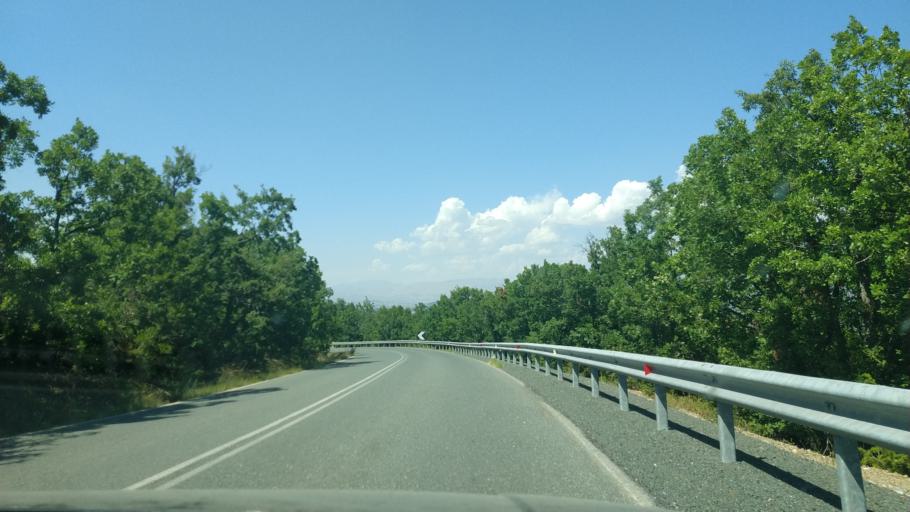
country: GR
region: West Macedonia
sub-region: Nomos Grevenon
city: Grevena
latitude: 40.0236
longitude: 21.4849
